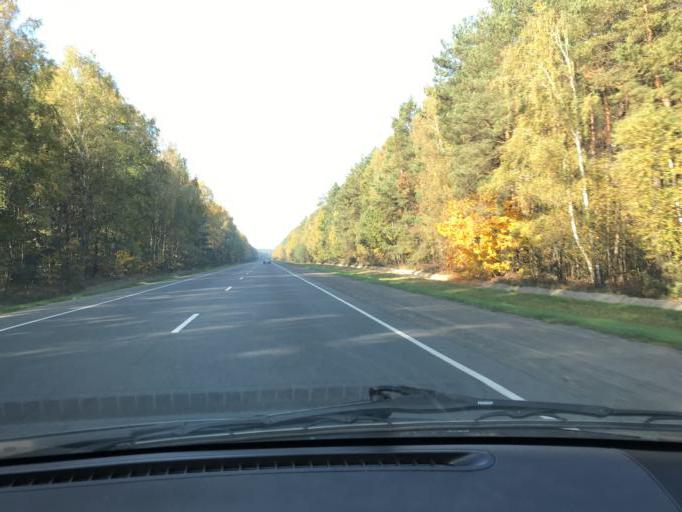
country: BY
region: Brest
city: Luninyets
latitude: 52.2766
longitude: 26.8621
